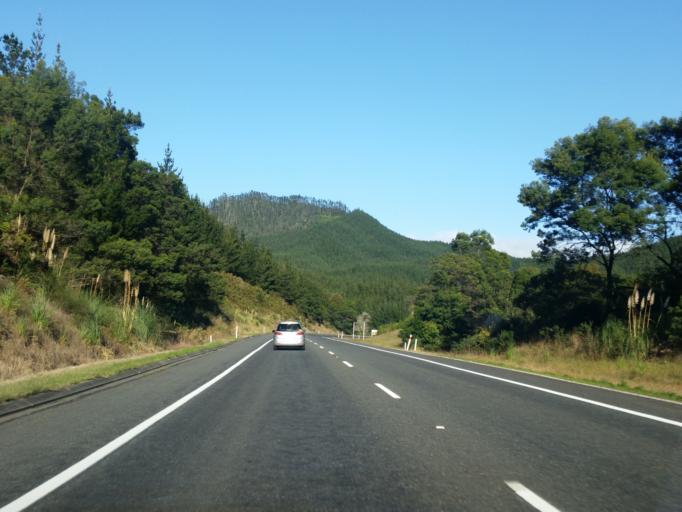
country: NZ
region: Bay of Plenty
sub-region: Western Bay of Plenty District
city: Waihi Beach
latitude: -37.4608
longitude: 175.9190
